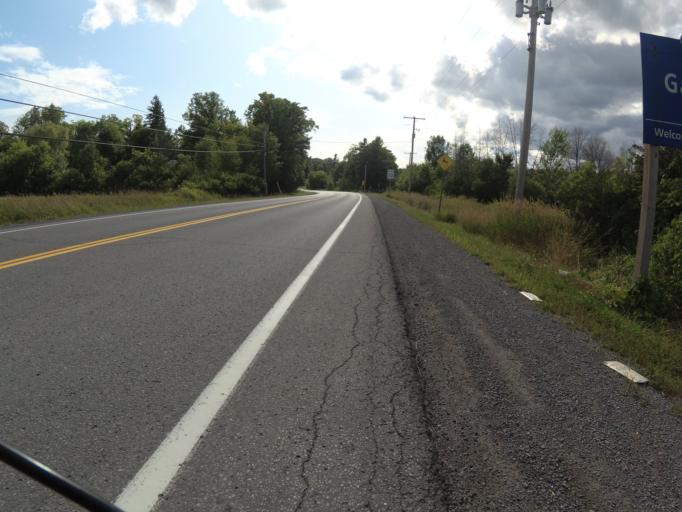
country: CA
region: Ontario
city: Arnprior
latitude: 45.4329
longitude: -76.2418
